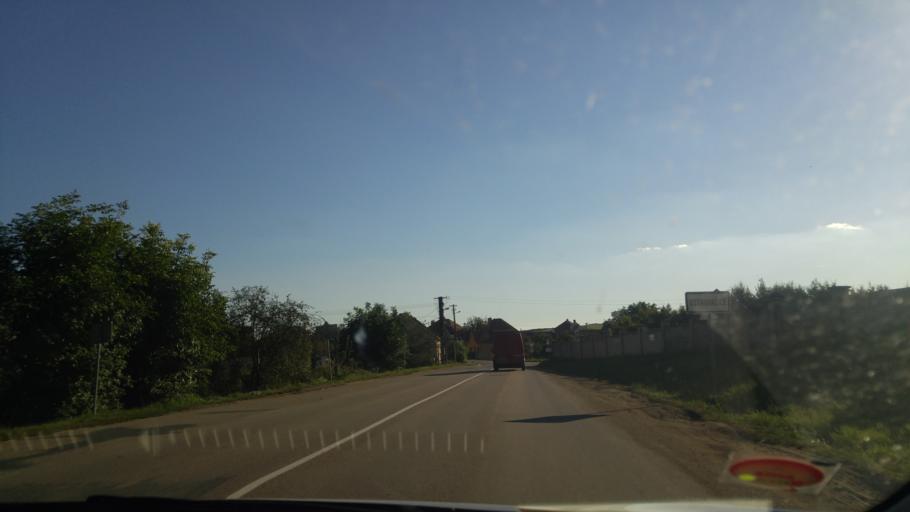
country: CZ
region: South Moravian
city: Ricany
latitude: 49.2140
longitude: 16.4085
